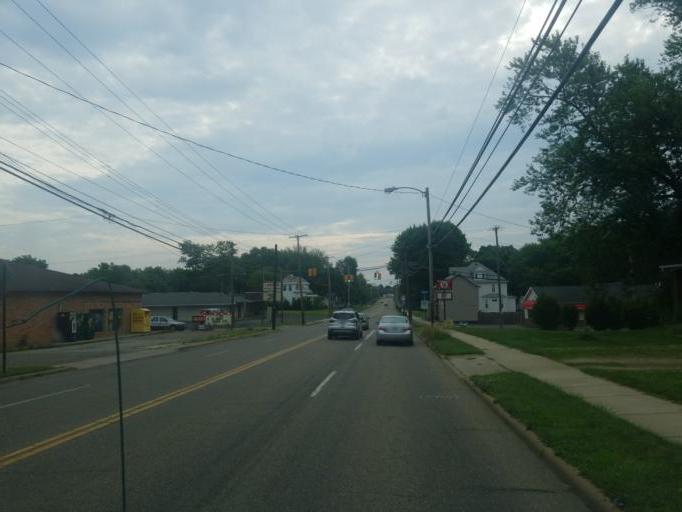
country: US
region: Ohio
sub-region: Stark County
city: Massillon
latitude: 40.7959
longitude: -81.5717
